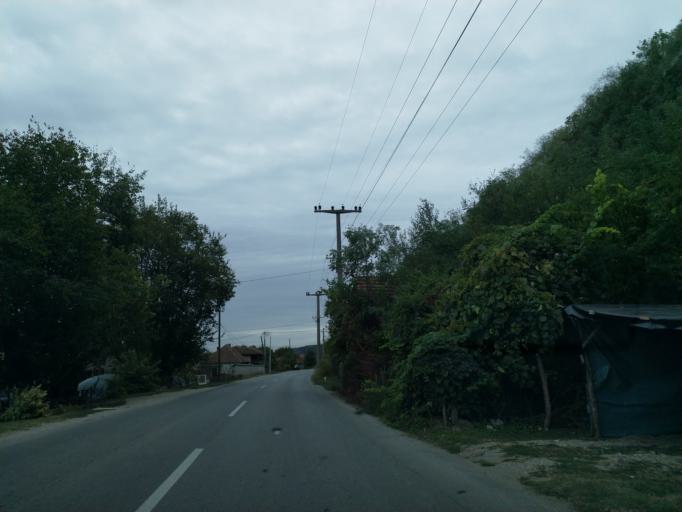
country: RS
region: Central Serbia
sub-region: Sumadijski Okrug
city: Batocina
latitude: 44.1050
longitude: 21.1609
